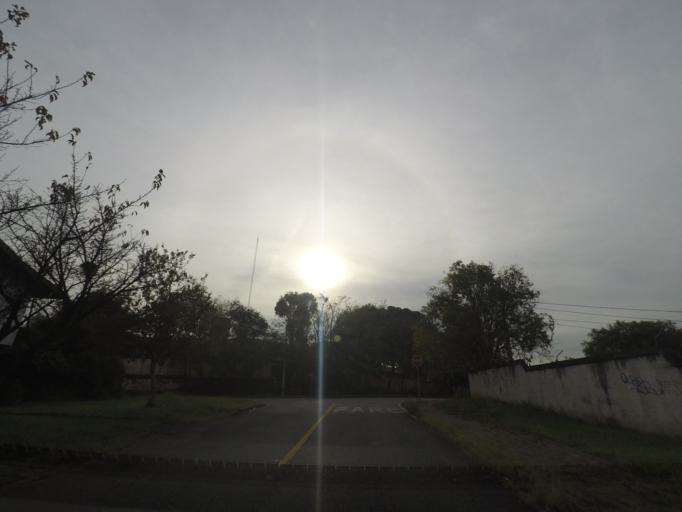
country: BR
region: Parana
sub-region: Curitiba
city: Curitiba
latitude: -25.4370
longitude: -49.2972
